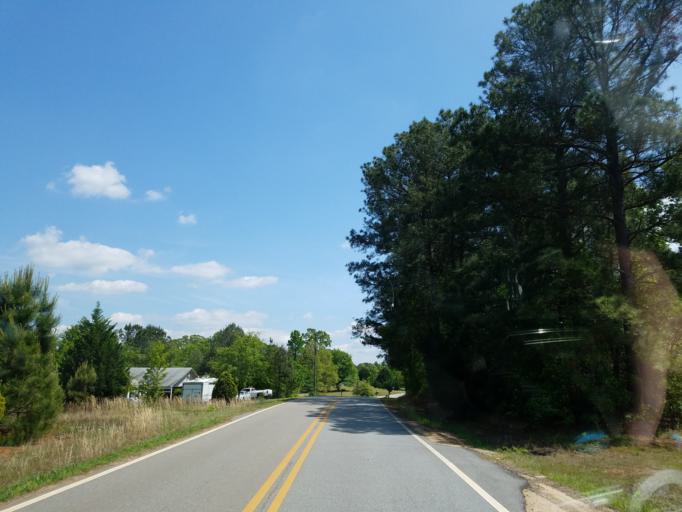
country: US
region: Georgia
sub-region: Butts County
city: Indian Springs
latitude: 33.1739
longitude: -84.0241
